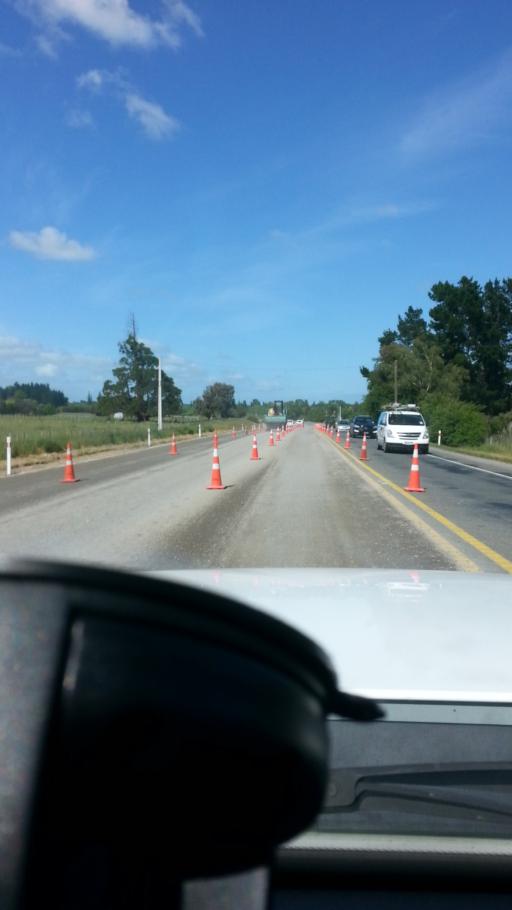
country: NZ
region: Wellington
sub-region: Masterton District
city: Masterton
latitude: -41.0486
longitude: 175.5016
